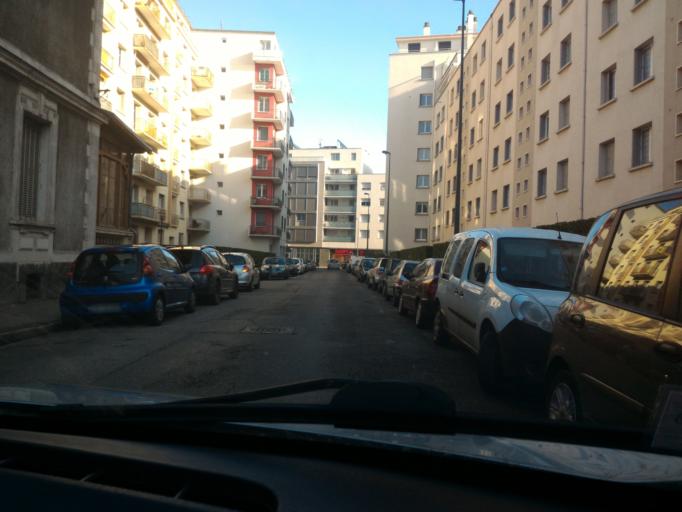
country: FR
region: Rhone-Alpes
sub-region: Departement de l'Isere
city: Grenoble
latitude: 45.1793
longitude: 5.7251
